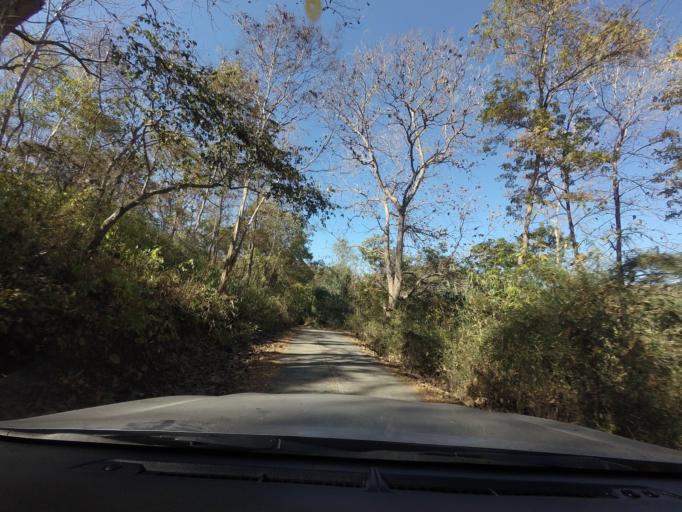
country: TH
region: Mae Hong Son
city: Wiang Nuea
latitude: 19.4024
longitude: 98.4177
